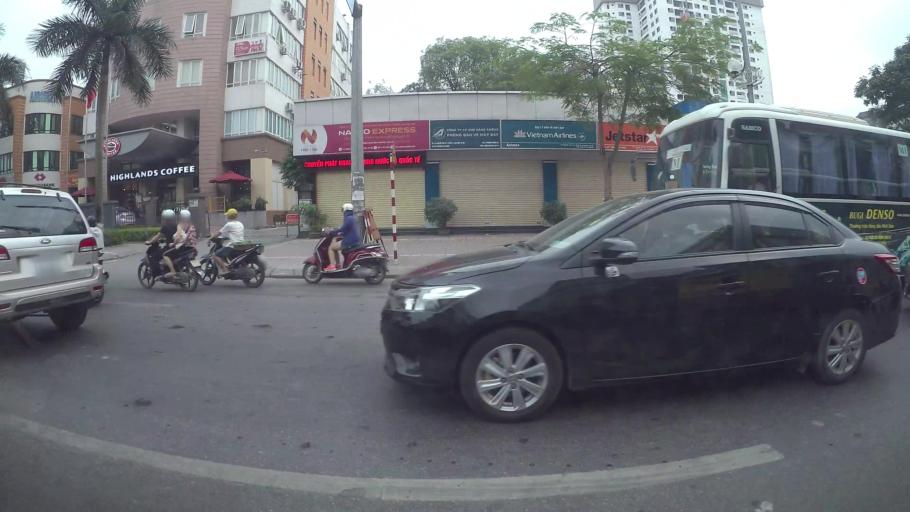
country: VN
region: Ha Noi
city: Hoan Kiem
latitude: 21.0467
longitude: 105.8778
